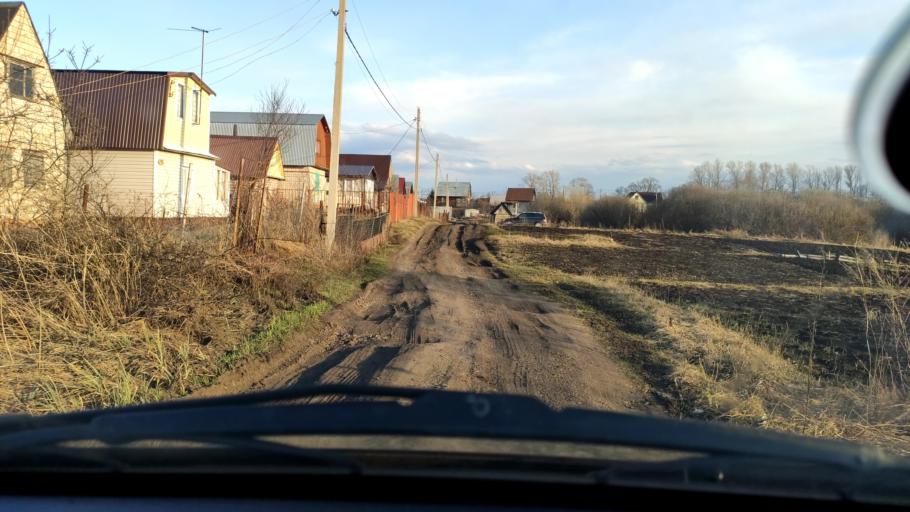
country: RU
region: Bashkortostan
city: Ufa
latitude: 54.5616
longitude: 55.9548
